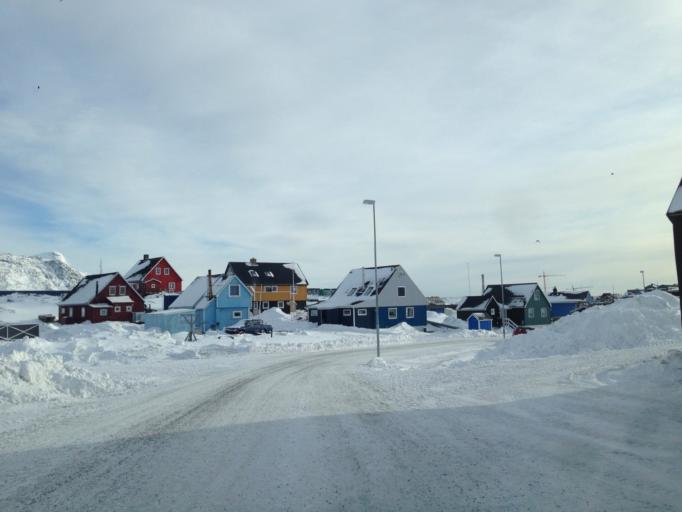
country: GL
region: Sermersooq
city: Nuuk
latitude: 64.1796
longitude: -51.7347
